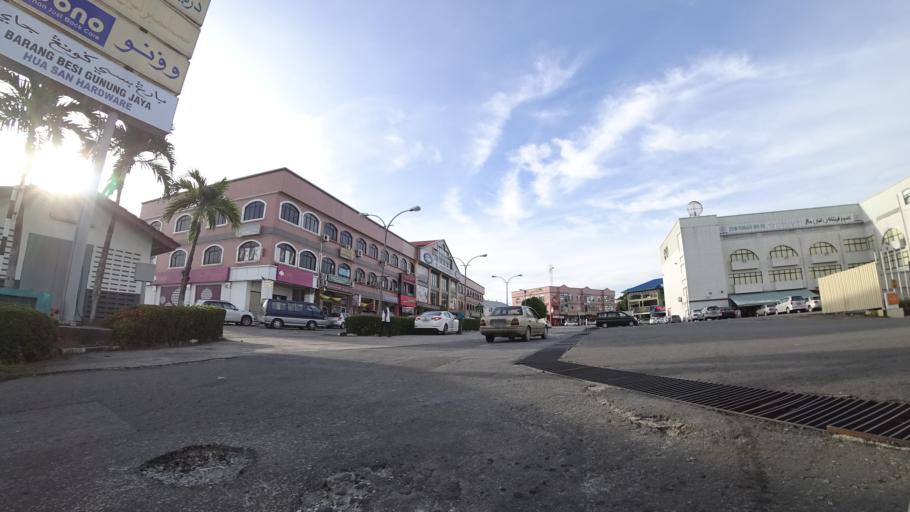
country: BN
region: Brunei and Muara
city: Bandar Seri Begawan
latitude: 4.8871
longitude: 114.8410
